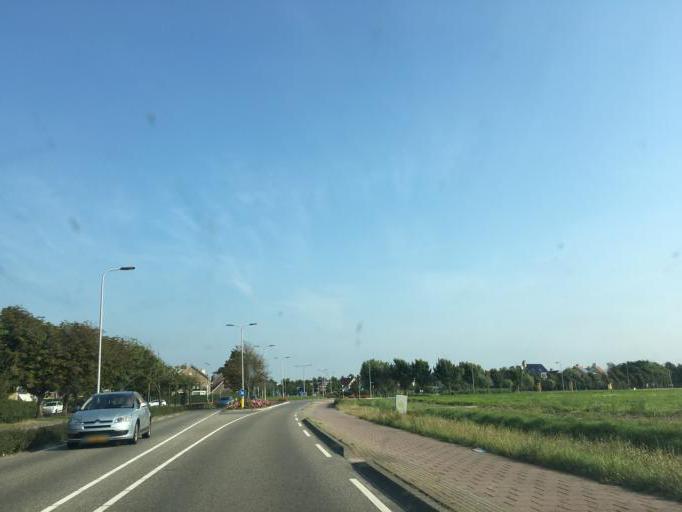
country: NL
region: South Holland
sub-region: Gemeente Noordwijk
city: Noordwijk-Binnen
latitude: 52.2345
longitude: 4.4369
